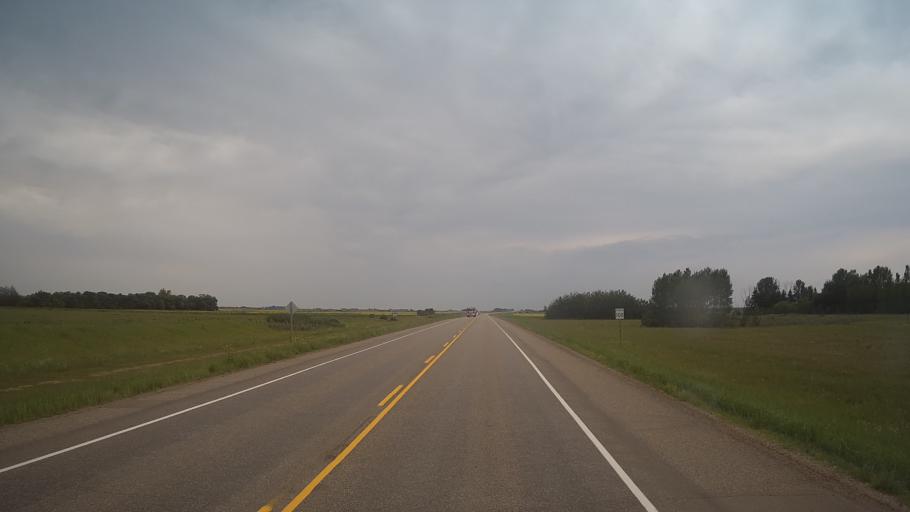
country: CA
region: Saskatchewan
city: Langham
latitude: 52.1287
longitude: -107.2361
